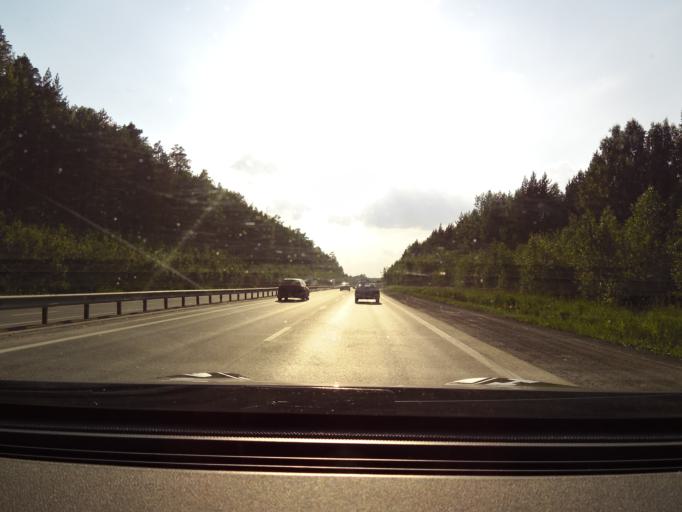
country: RU
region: Sverdlovsk
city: Severka
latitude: 56.8338
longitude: 60.3051
